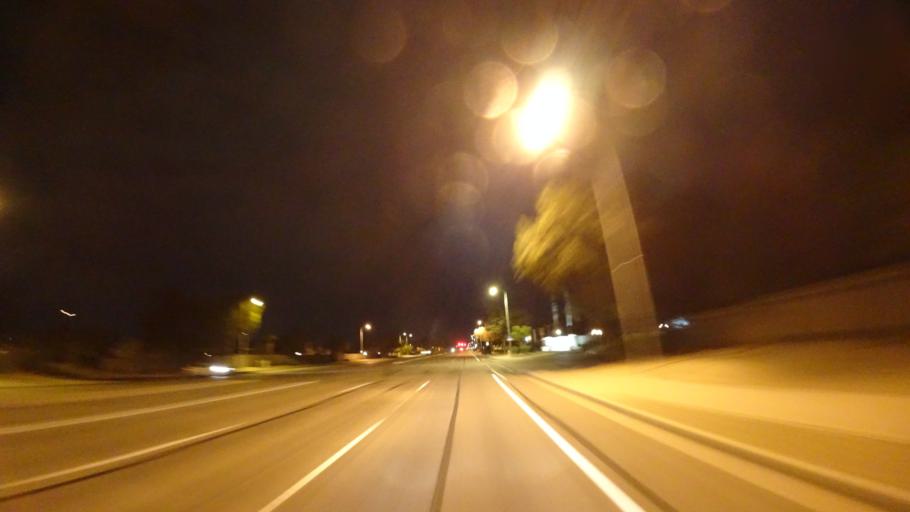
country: US
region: Arizona
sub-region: Maricopa County
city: Chandler
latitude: 33.2914
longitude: -111.8638
